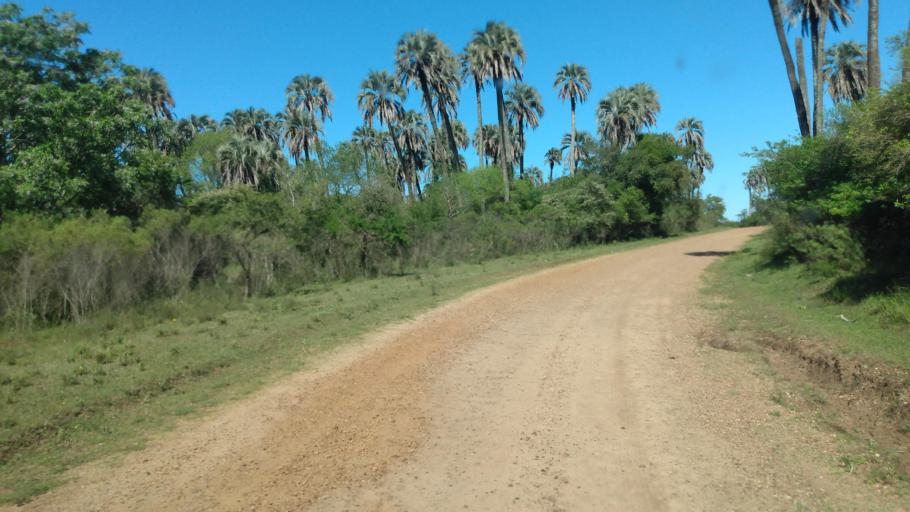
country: AR
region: Entre Rios
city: Ubajay
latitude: -31.8763
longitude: -58.2332
